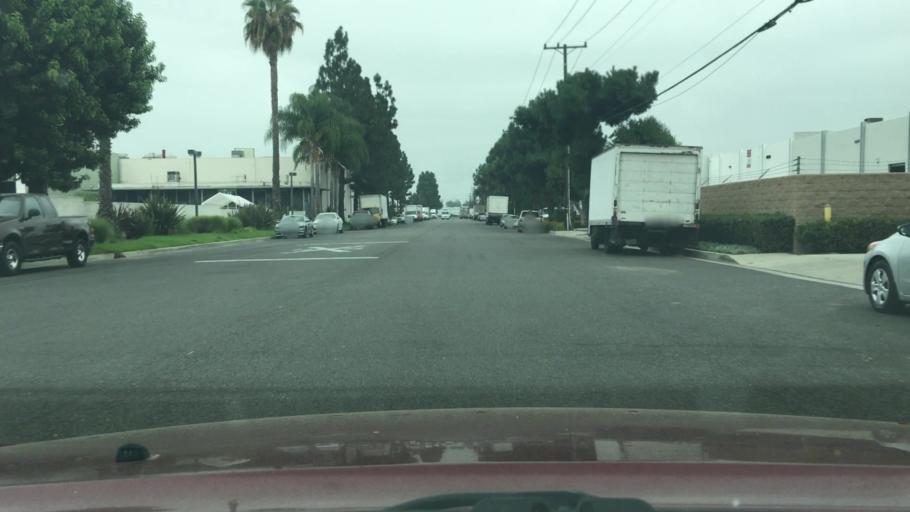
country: US
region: California
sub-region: Orange County
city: Buena Park
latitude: 33.8857
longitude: -118.0216
